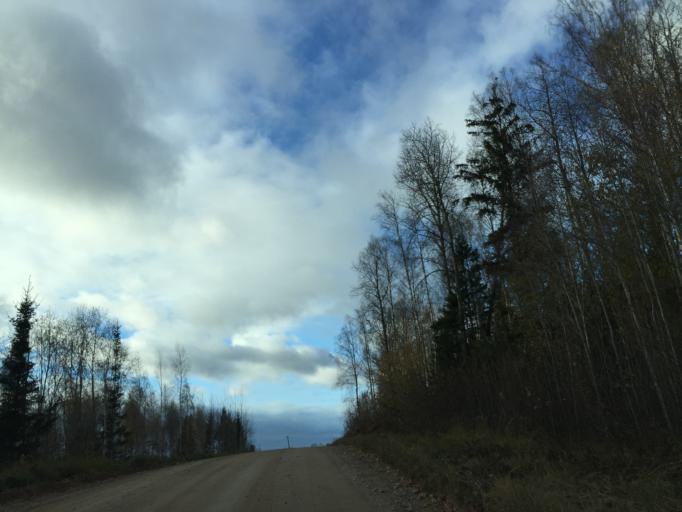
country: LV
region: Tukuma Rajons
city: Tukums
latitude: 56.9812
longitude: 23.0054
